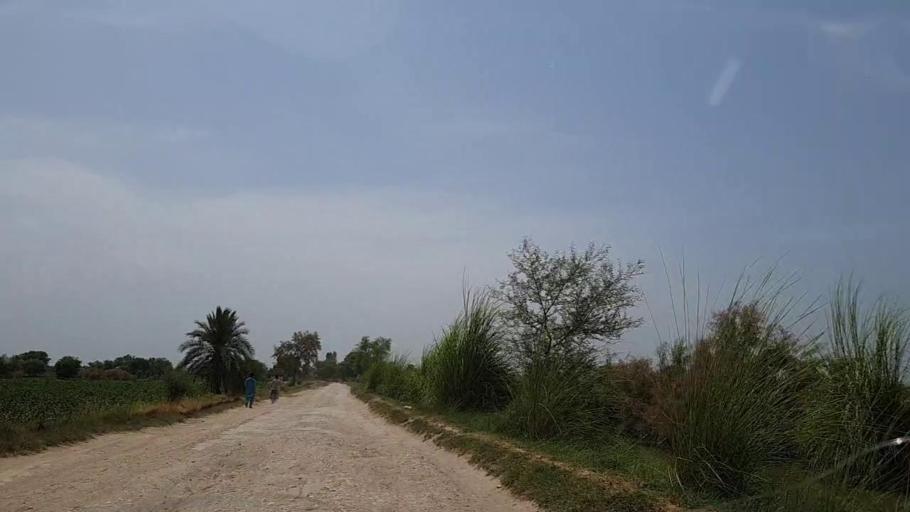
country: PK
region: Sindh
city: Khanpur
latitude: 27.8550
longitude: 69.4864
